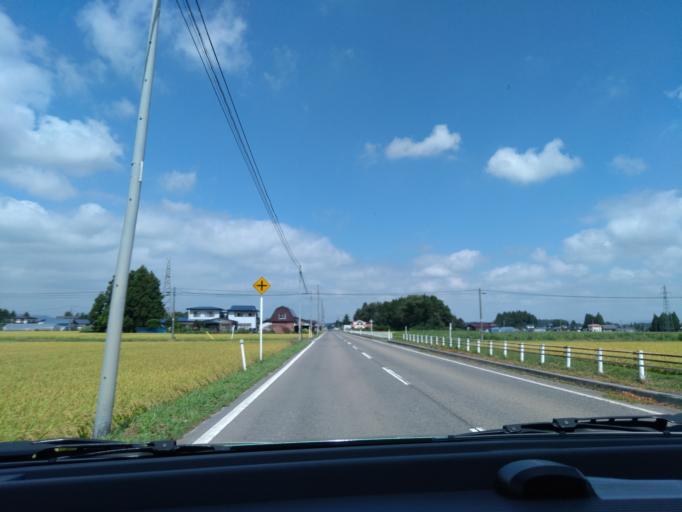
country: JP
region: Iwate
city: Kitakami
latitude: 39.3037
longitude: 141.0508
